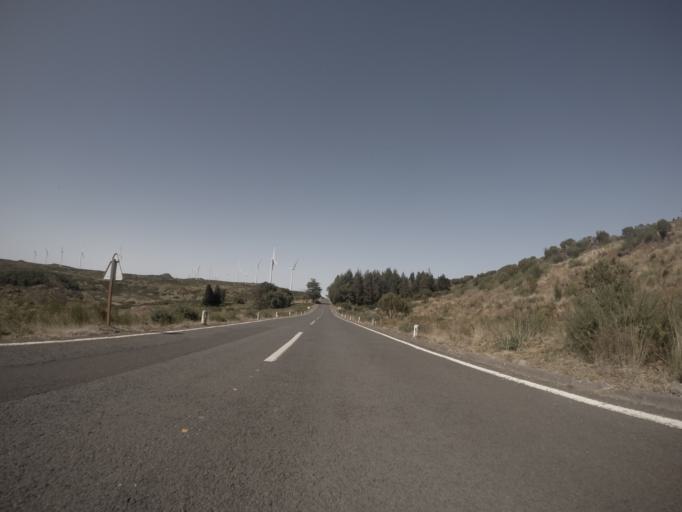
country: PT
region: Madeira
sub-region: Sao Vicente
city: Sao Vicente
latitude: 32.7537
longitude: -17.0587
